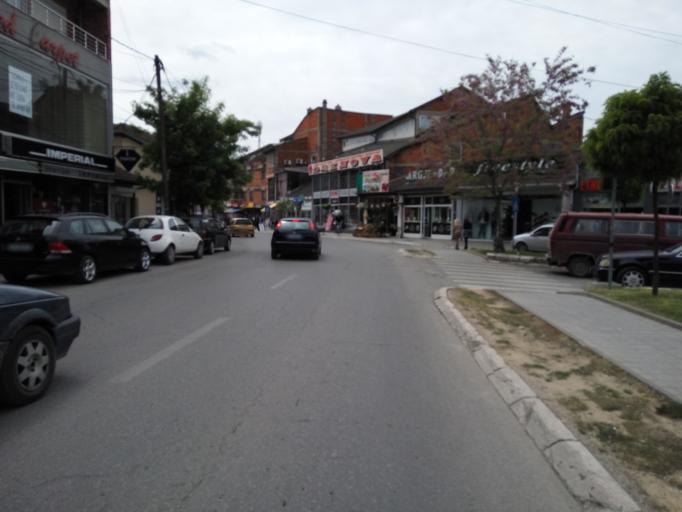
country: XK
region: Gjakova
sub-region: Komuna e Gjakoves
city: Gjakove
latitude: 42.3787
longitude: 20.4310
